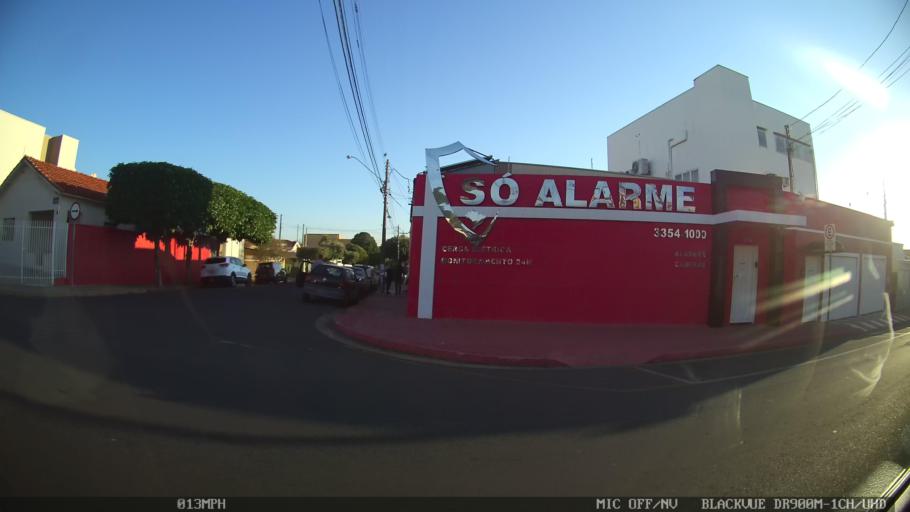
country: BR
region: Sao Paulo
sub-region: Sao Jose Do Rio Preto
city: Sao Jose do Rio Preto
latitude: -20.7975
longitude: -49.3900
